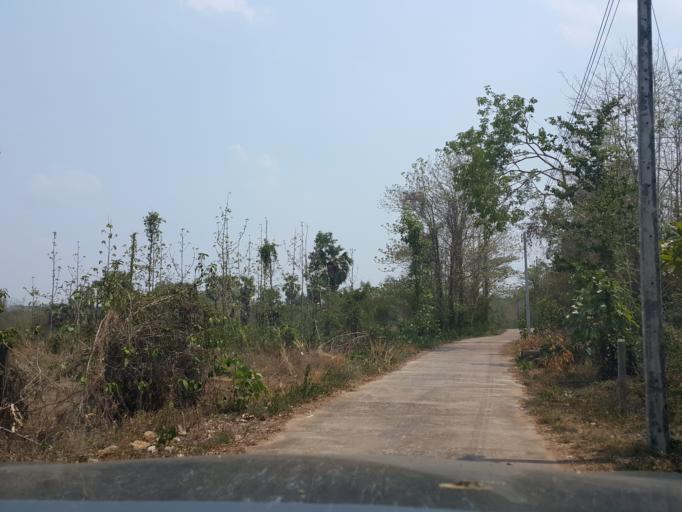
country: TH
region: Lampang
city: Mae Phrik
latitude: 17.5703
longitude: 99.0863
